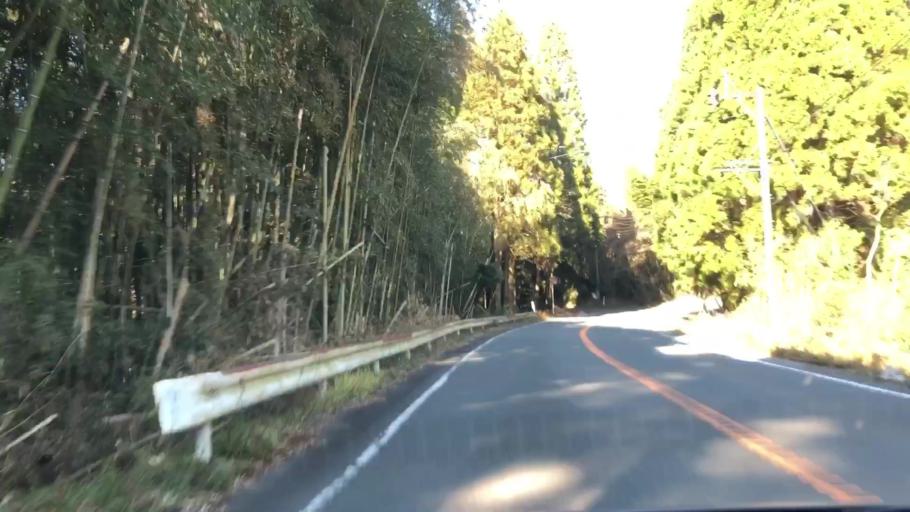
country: JP
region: Kagoshima
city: Satsumasendai
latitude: 31.8562
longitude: 130.4294
